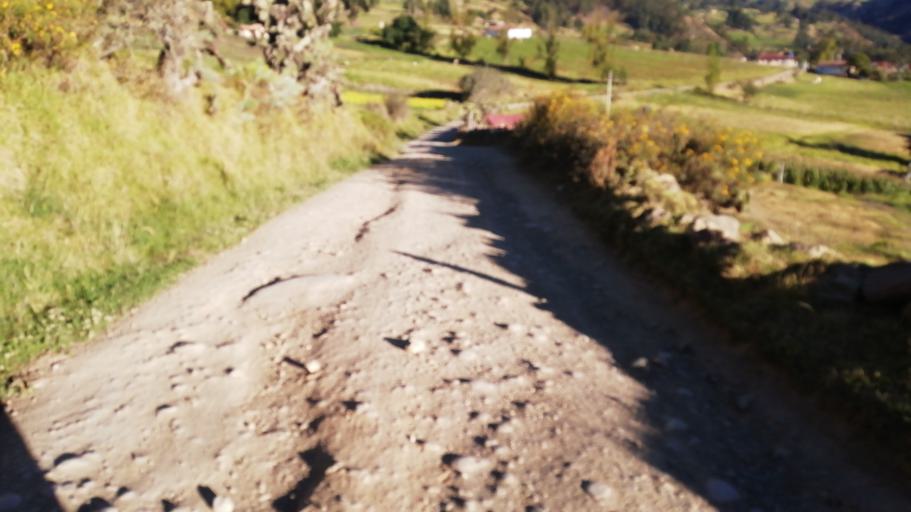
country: CO
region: Boyaca
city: Gameza
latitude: 5.7932
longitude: -72.8042
